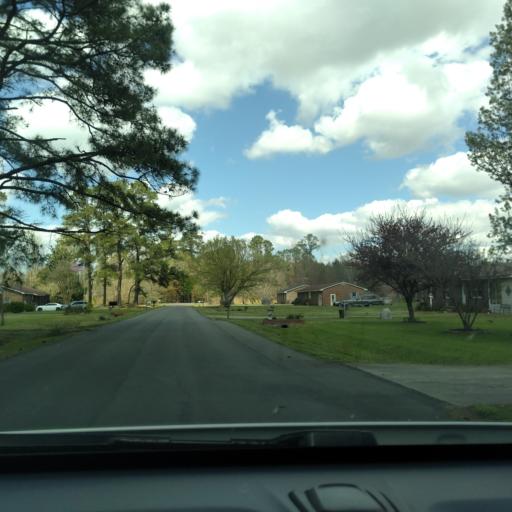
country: US
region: North Carolina
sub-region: Washington County
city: Plymouth
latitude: 35.8277
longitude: -76.7717
